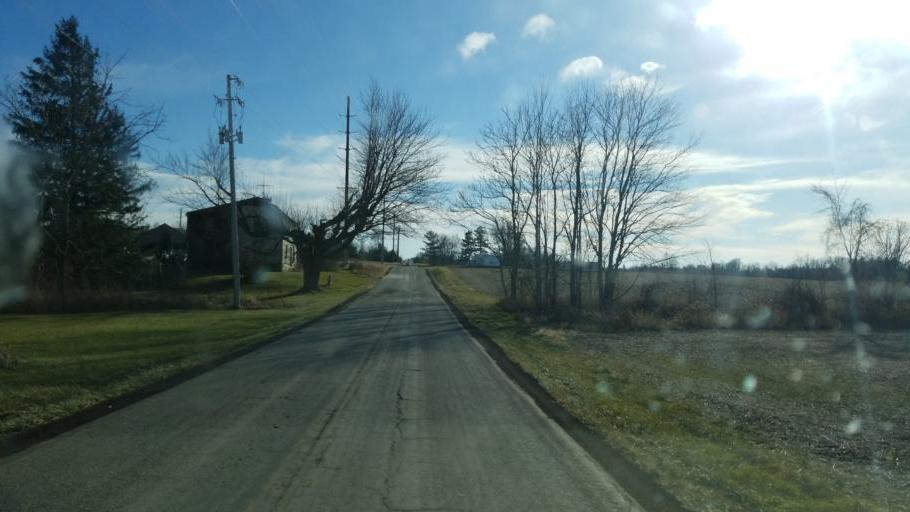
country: US
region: Ohio
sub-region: Crawford County
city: Crestline
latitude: 40.7734
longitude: -82.6981
